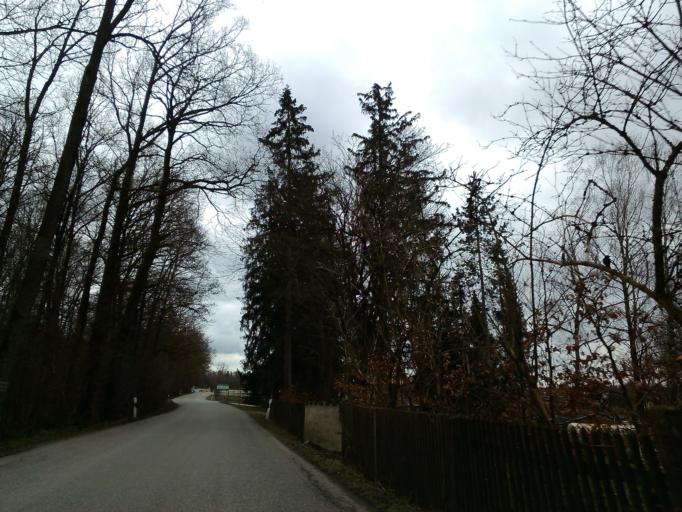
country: DE
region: Bavaria
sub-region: Upper Bavaria
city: Gauting
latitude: 48.0856
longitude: 11.3411
